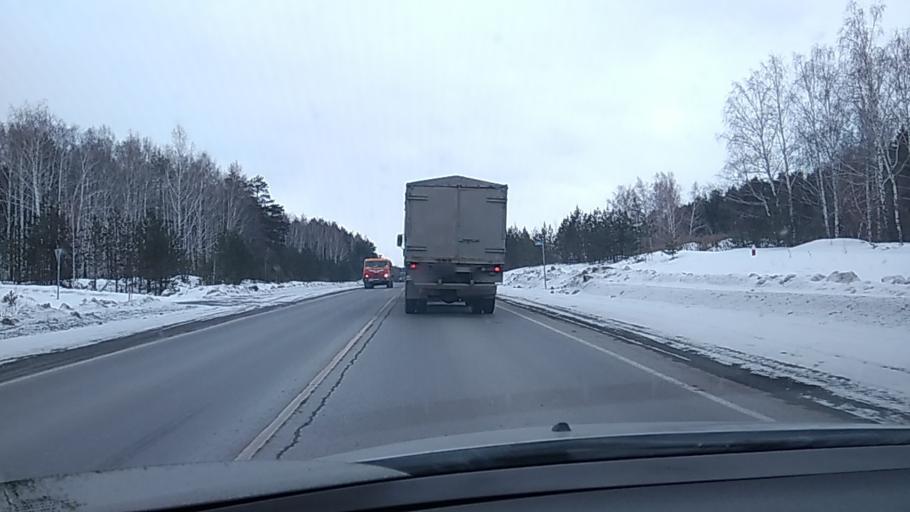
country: RU
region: Sverdlovsk
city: Verkhneye Dubrovo
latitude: 56.7157
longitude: 61.0574
